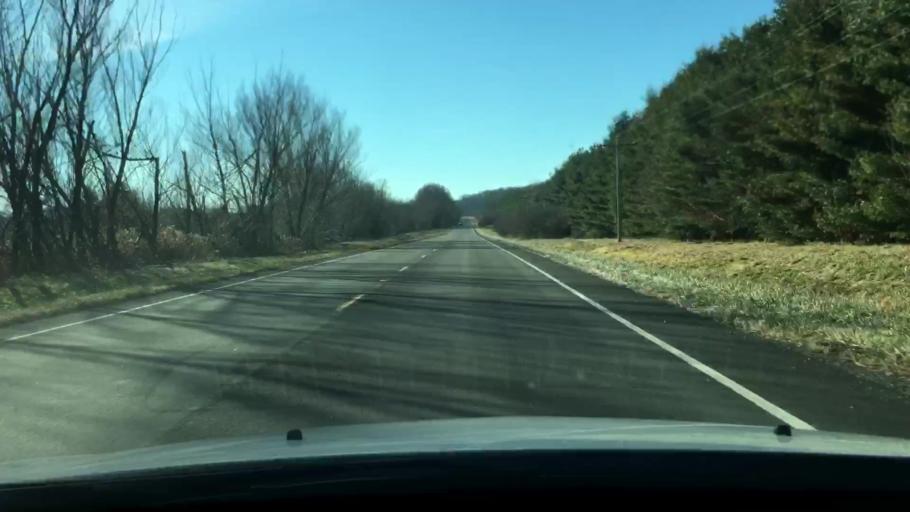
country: US
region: Illinois
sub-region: Fulton County
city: Canton
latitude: 40.4948
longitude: -89.9361
